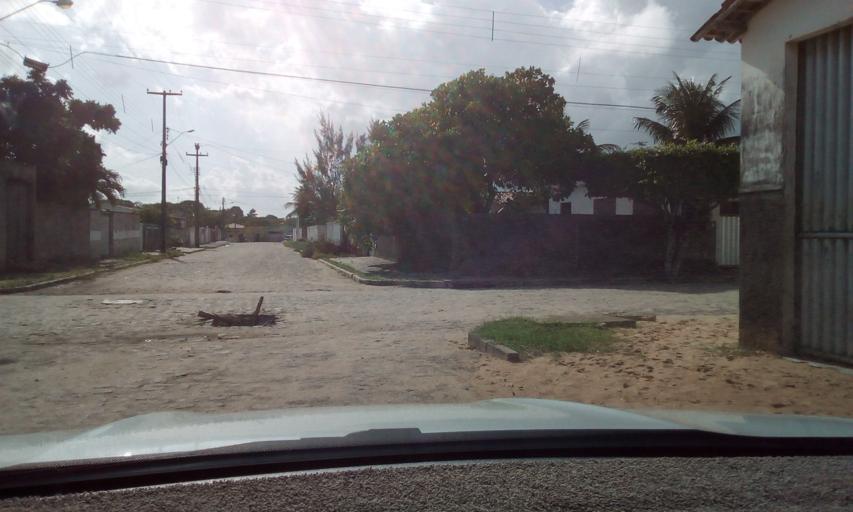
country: BR
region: Paraiba
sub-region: Joao Pessoa
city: Joao Pessoa
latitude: -7.1839
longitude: -34.8253
